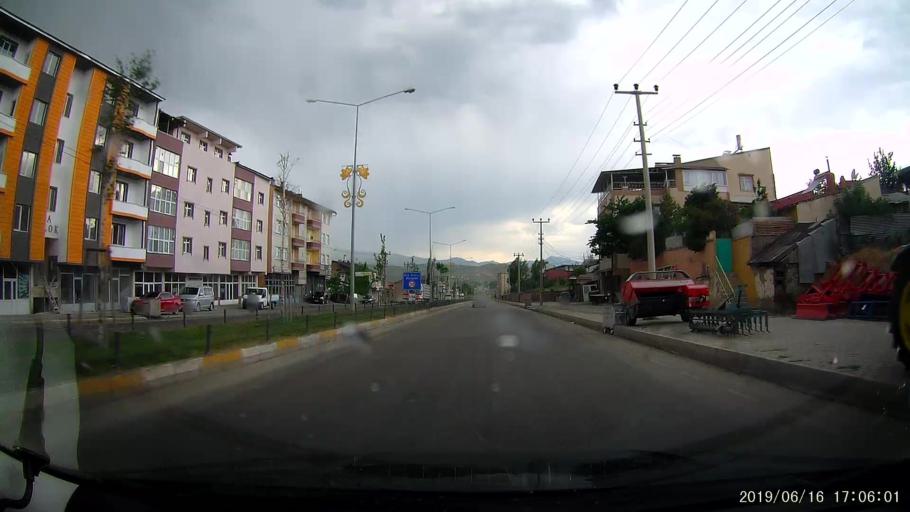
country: TR
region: Erzurum
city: Askale
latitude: 39.9198
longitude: 40.6919
